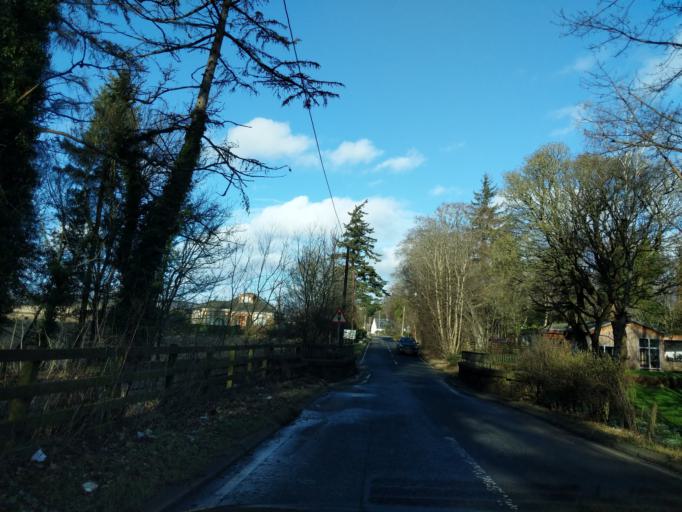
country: GB
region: Scotland
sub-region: West Lothian
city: Kirknewton
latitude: 55.8993
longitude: -3.3974
